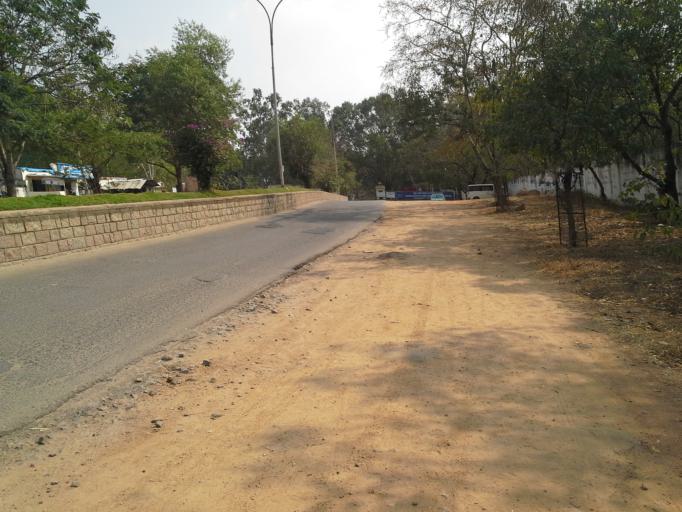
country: IN
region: Telangana
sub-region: Hyderabad
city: Hyderabad
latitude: 17.3173
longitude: 78.4038
